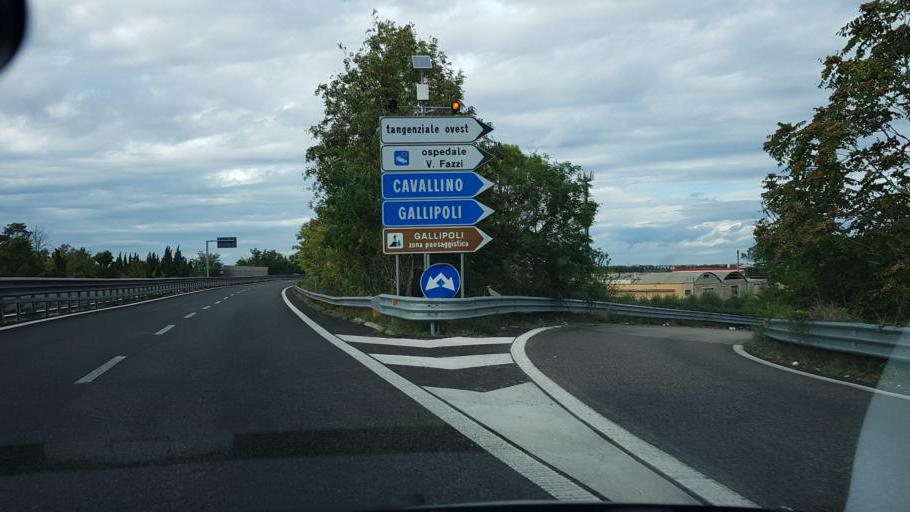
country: IT
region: Apulia
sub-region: Provincia di Lecce
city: Castromediano
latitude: 40.3245
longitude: 18.1855
